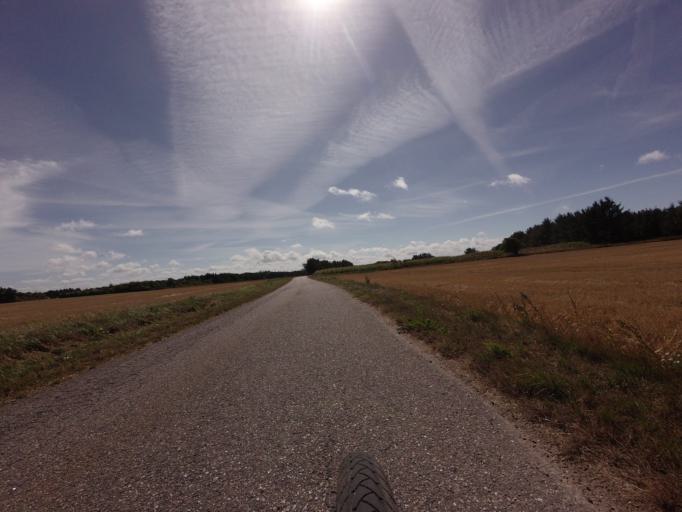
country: DK
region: North Denmark
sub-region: Hjorring Kommune
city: Vra
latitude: 57.3819
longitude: 9.7835
